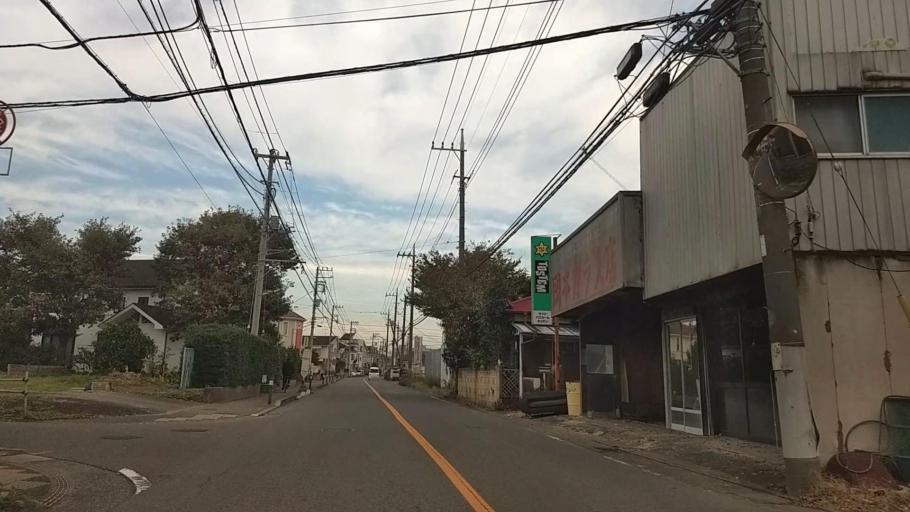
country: JP
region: Kanagawa
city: Fujisawa
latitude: 35.3936
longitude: 139.4418
